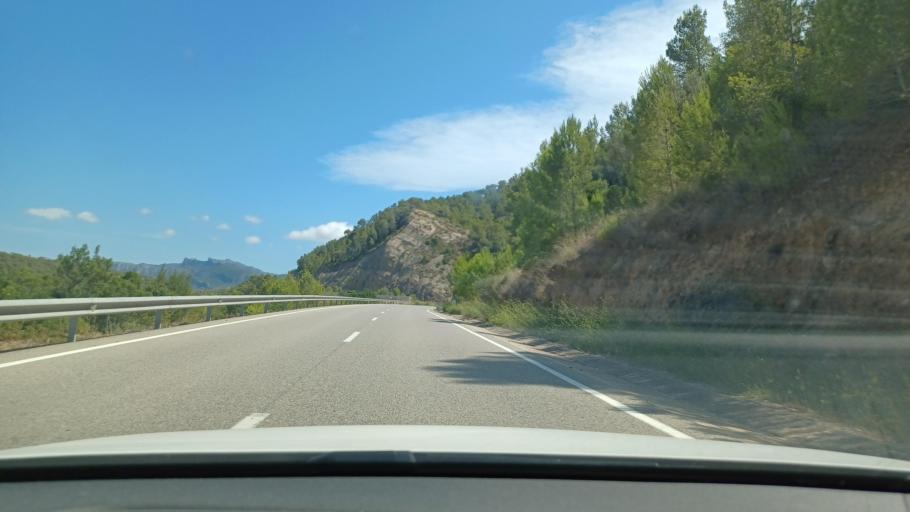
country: ES
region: Catalonia
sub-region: Provincia de Tarragona
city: Benifallet
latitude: 40.9520
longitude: 0.4490
